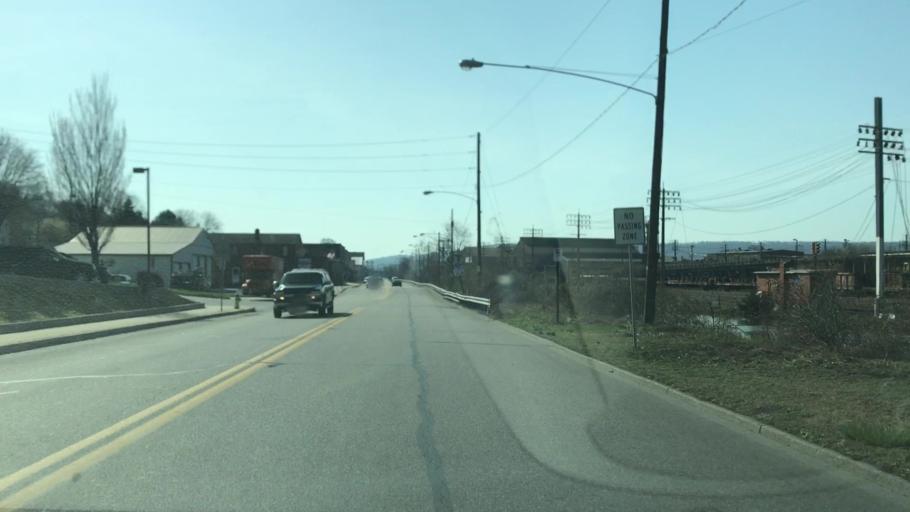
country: US
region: Pennsylvania
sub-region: Dauphin County
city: Enhaut
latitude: 40.2299
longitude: -76.8335
